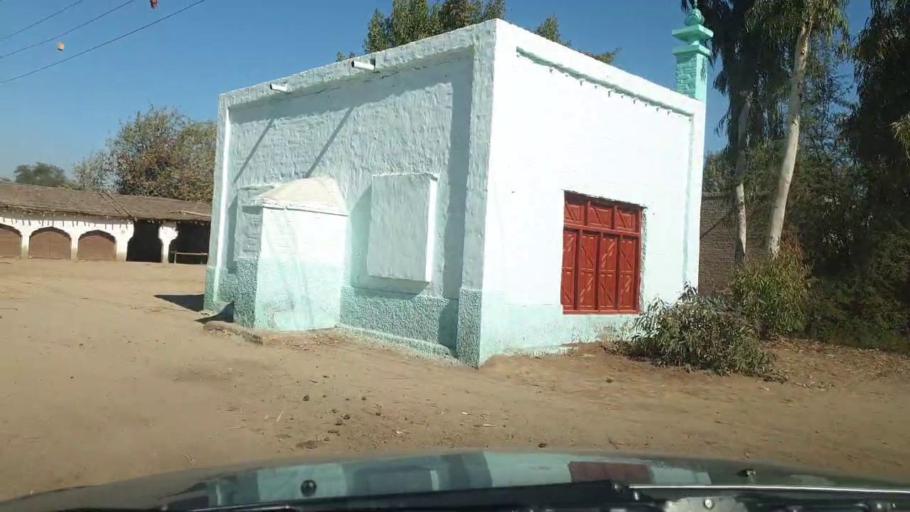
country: PK
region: Sindh
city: Ghotki
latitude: 28.0521
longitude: 69.2298
